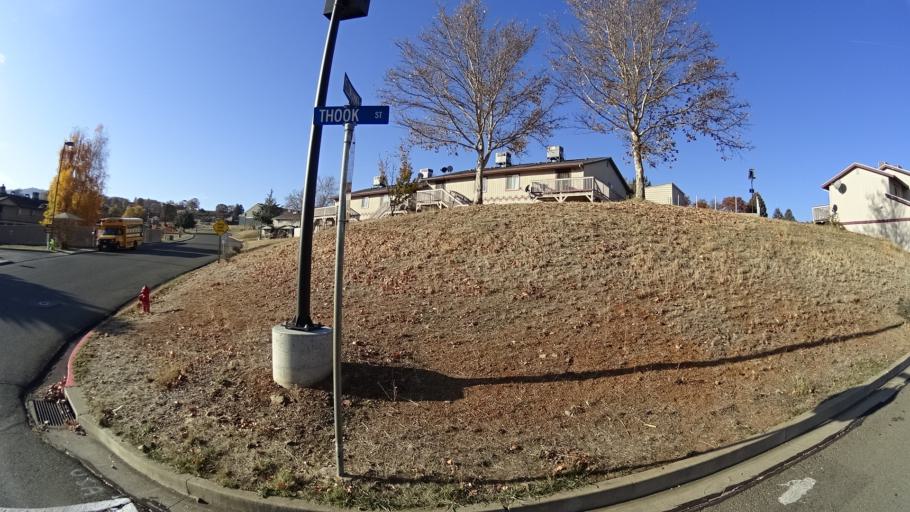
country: US
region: California
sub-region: Siskiyou County
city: Yreka
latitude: 41.7131
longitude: -122.6255
